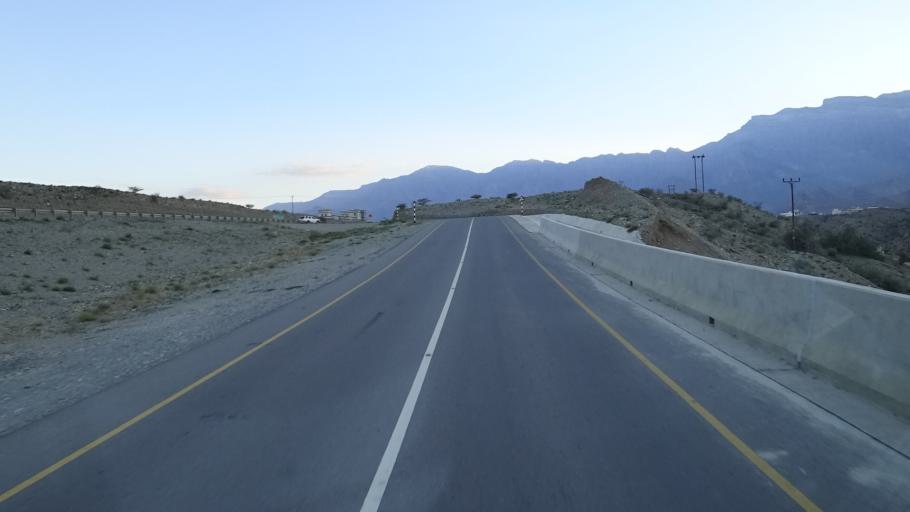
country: OM
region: Al Batinah
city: Rustaq
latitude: 23.2839
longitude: 57.3336
